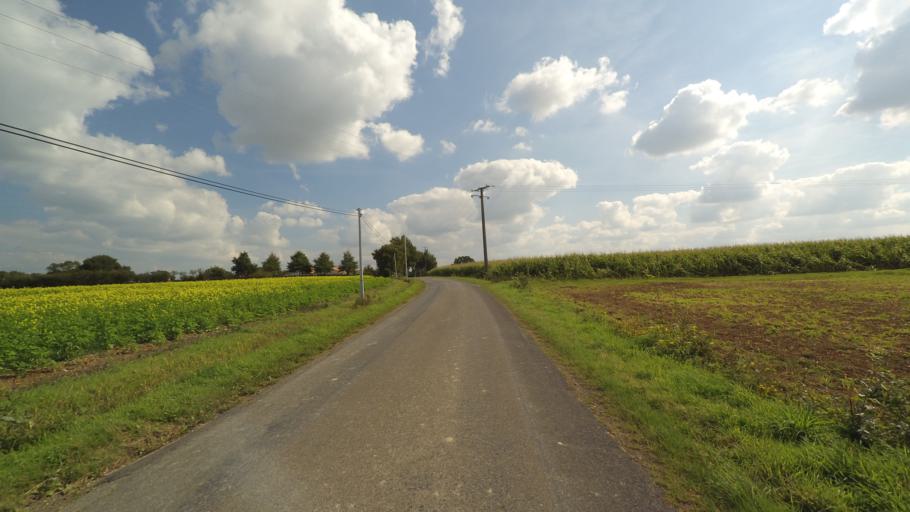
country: FR
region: Pays de la Loire
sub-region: Departement de la Vendee
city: Bouffere
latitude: 46.9555
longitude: -1.3777
